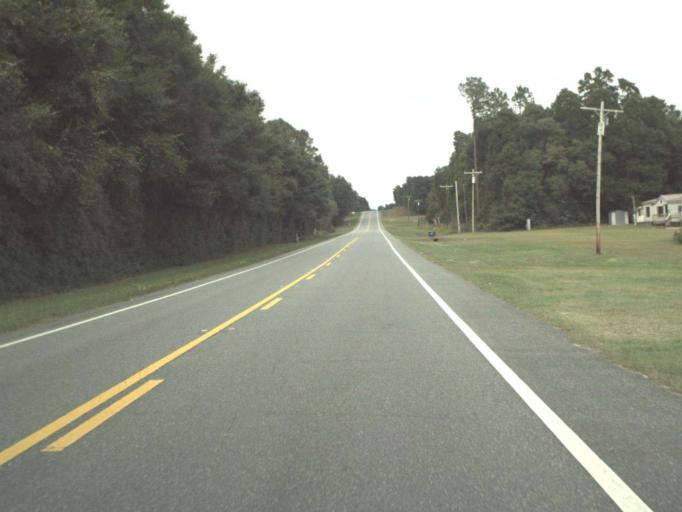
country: US
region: Florida
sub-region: Calhoun County
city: Blountstown
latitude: 30.5476
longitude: -85.1883
